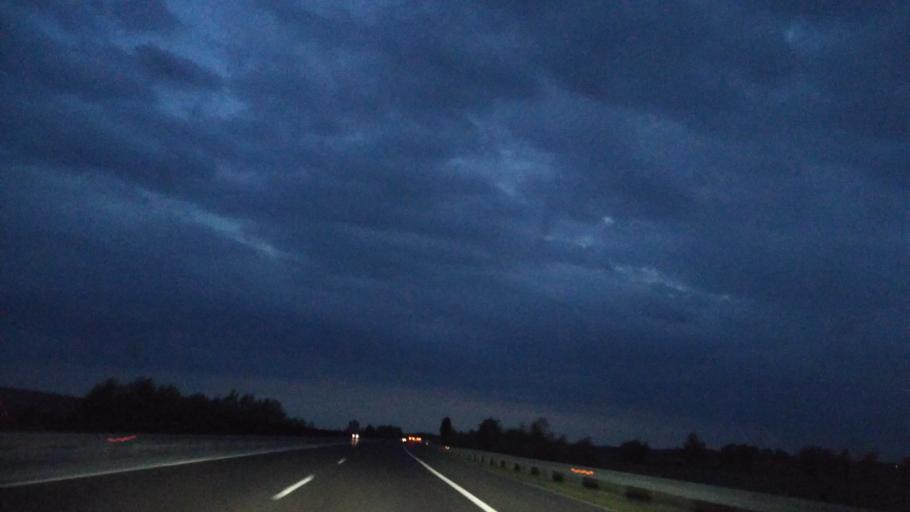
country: HU
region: Somogy
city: Fonyod
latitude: 46.7098
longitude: 17.5699
